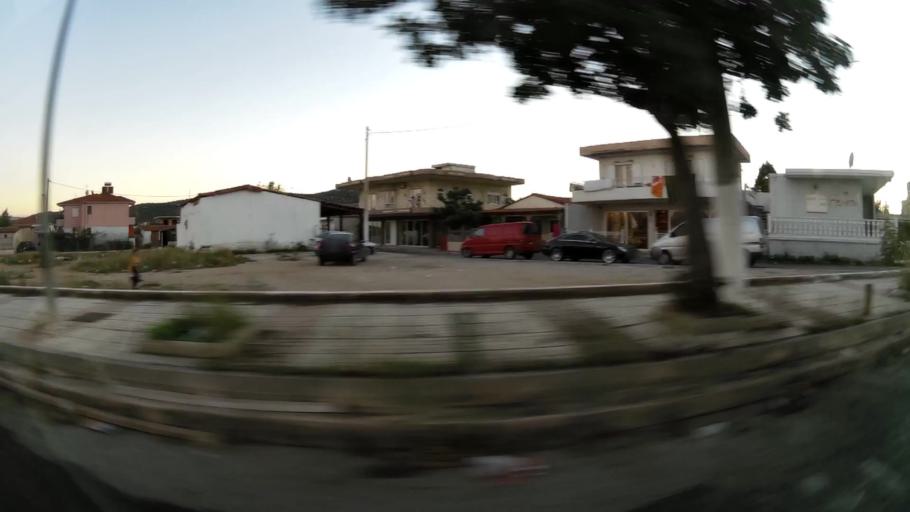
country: GR
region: Attica
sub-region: Nomarchia Dytikis Attikis
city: Ano Liosia
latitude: 38.0812
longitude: 23.6940
